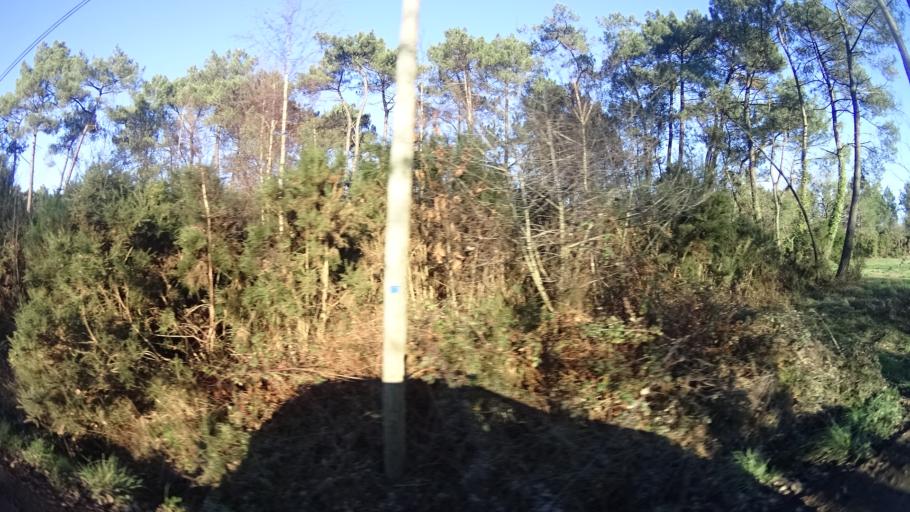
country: FR
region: Brittany
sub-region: Departement du Morbihan
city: Allaire
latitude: 47.6605
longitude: -2.1766
